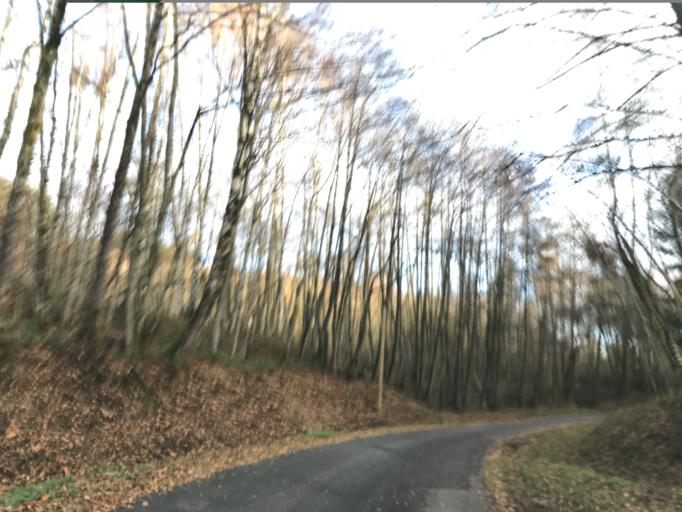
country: FR
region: Auvergne
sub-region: Departement du Puy-de-Dome
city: Celles-sur-Durolle
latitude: 45.7771
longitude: 3.6543
